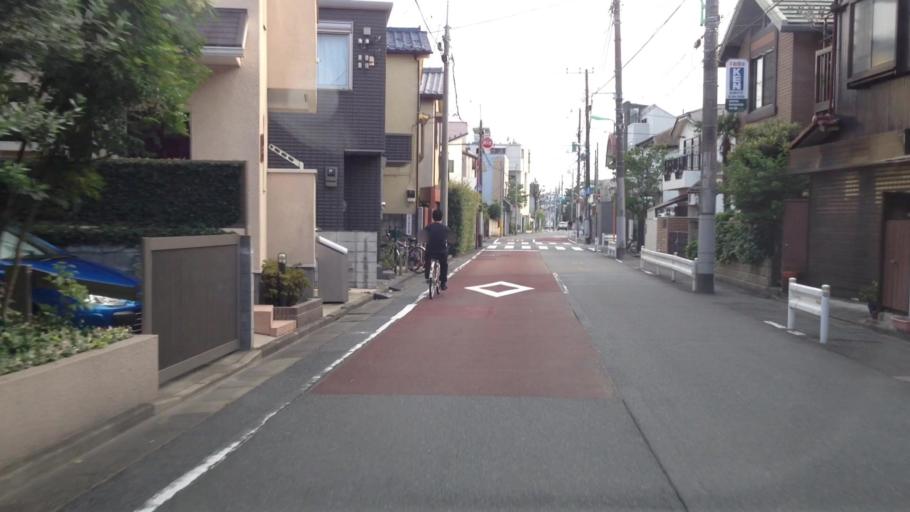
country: JP
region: Tokyo
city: Tokyo
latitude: 35.6343
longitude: 139.6841
